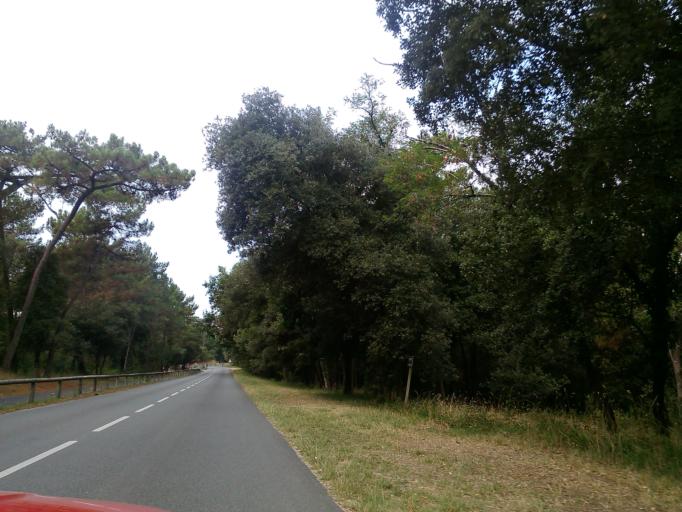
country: FR
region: Poitou-Charentes
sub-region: Departement de la Charente-Maritime
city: La Tremblade
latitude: 45.7888
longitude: -1.1897
